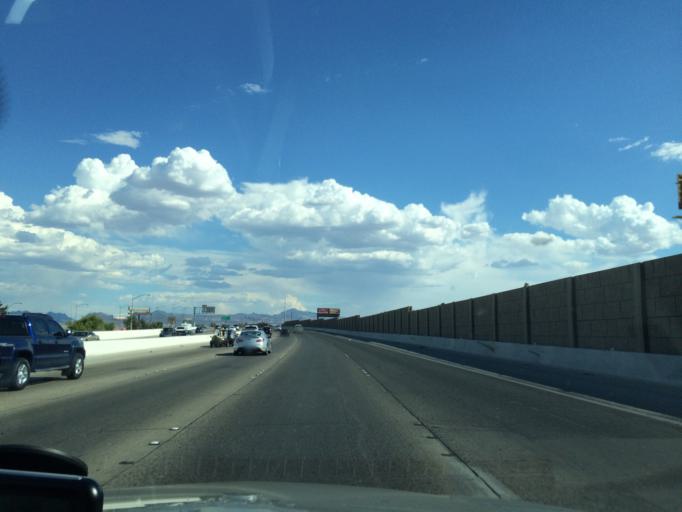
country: US
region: Nevada
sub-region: Clark County
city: Winchester
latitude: 36.1331
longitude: -115.0901
